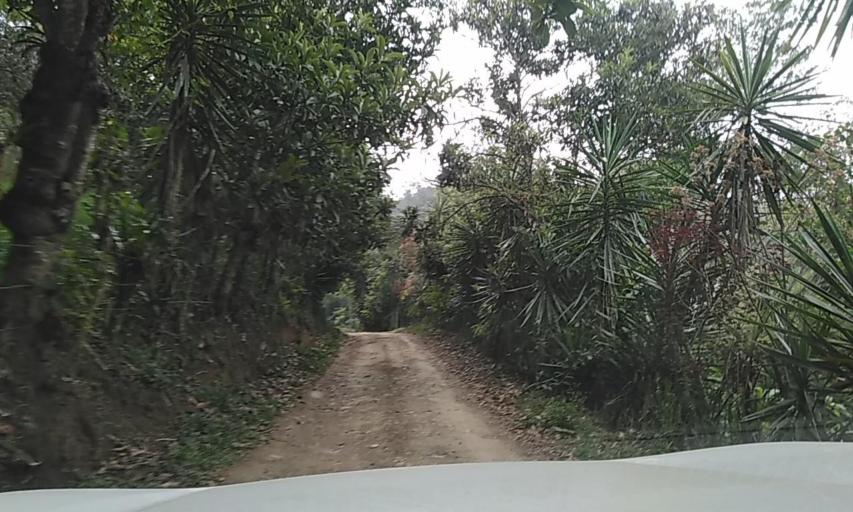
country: MX
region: Veracruz
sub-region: Xalapa
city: Lomas Verdes
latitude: 19.4999
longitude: -96.9176
